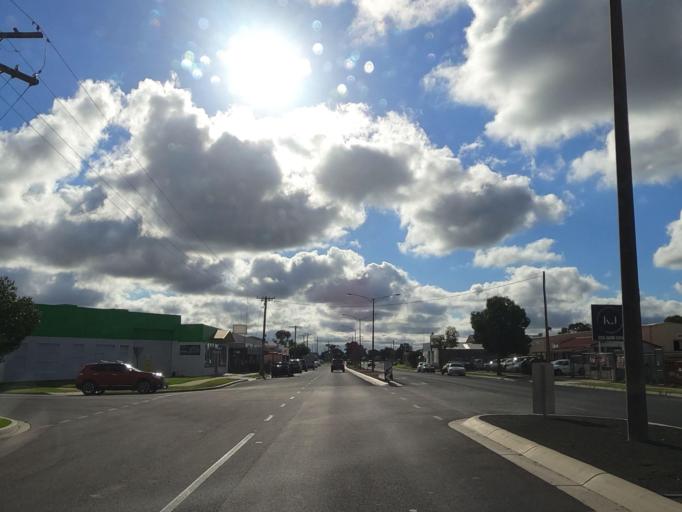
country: AU
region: Victoria
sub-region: Swan Hill
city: Swan Hill
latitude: -35.3309
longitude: 143.5549
